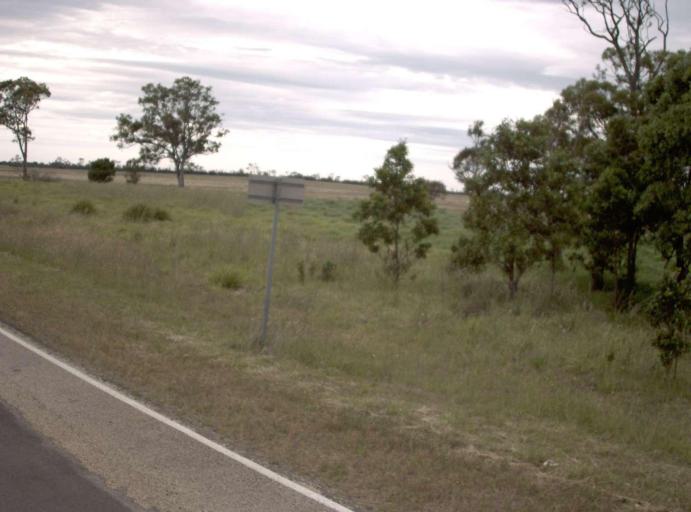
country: AU
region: Victoria
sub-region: East Gippsland
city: Bairnsdale
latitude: -37.9512
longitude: 147.5183
